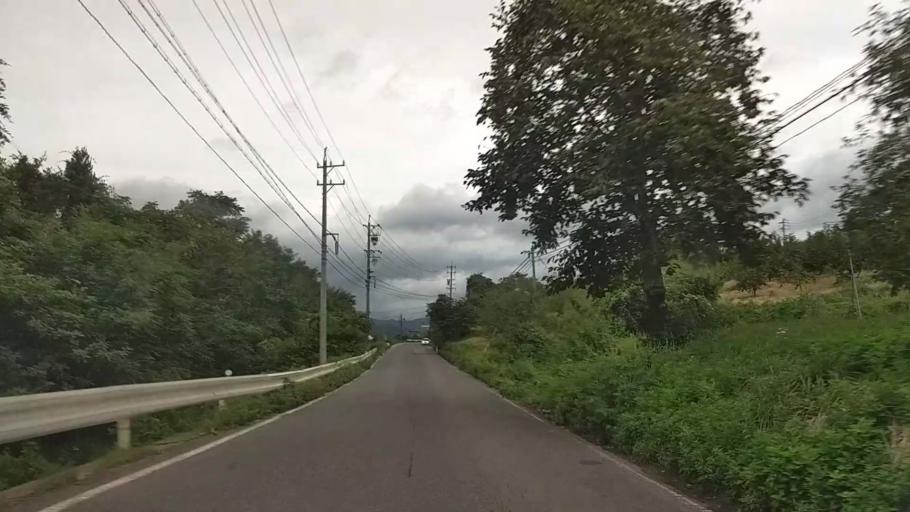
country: JP
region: Nagano
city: Iiyama
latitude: 36.8093
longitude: 138.3604
